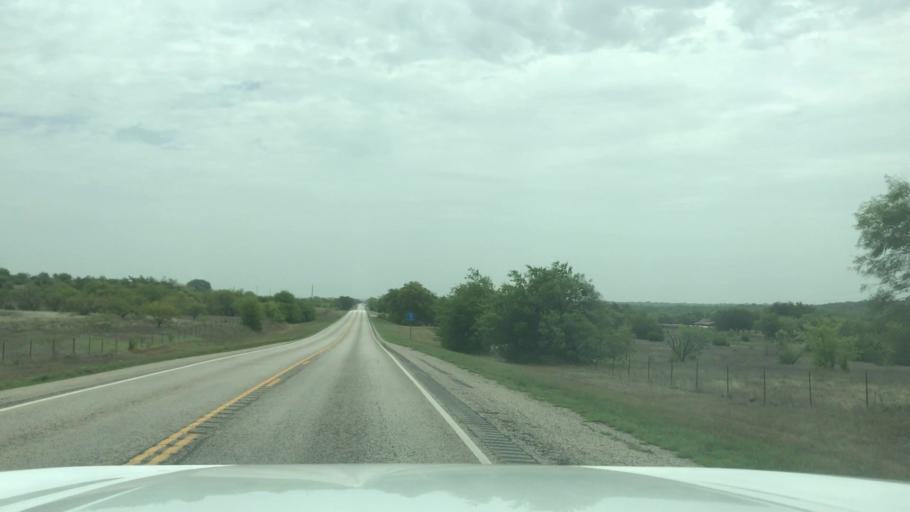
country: US
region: Texas
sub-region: Hamilton County
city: Hico
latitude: 32.0510
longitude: -98.1638
